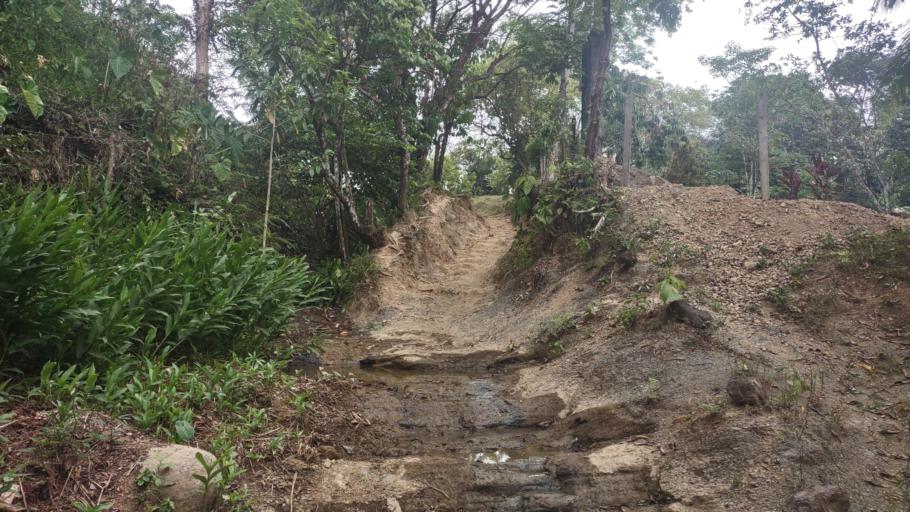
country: MX
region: Tabasco
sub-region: Huimanguillo
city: Francisco Rueda
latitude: 17.4426
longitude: -94.0223
